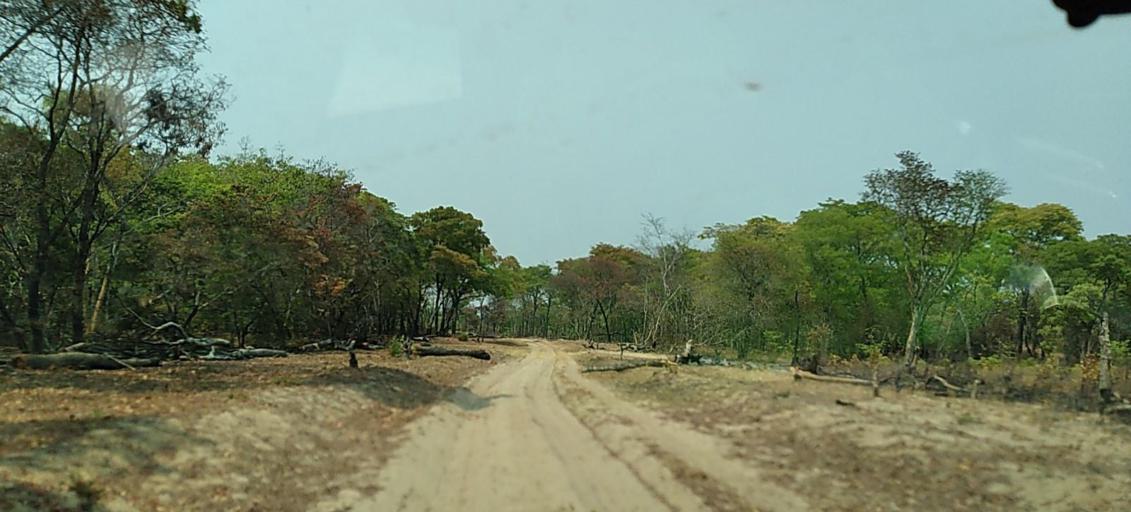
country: ZM
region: Western
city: Lukulu
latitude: -13.9584
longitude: 23.2247
